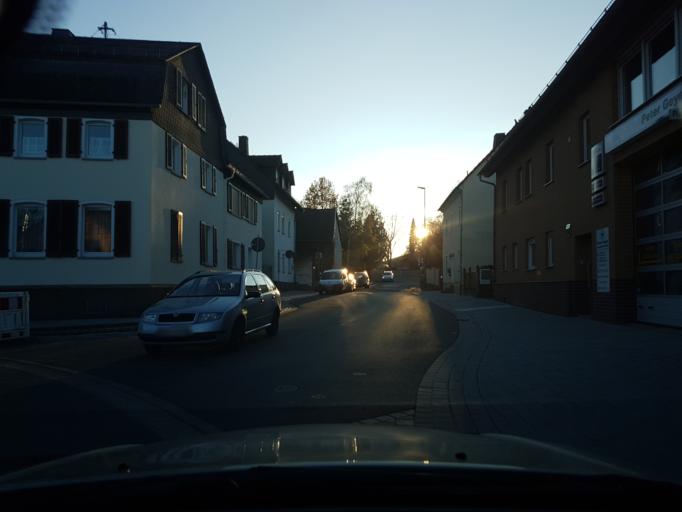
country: DE
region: Hesse
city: Taunusstein
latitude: 50.1538
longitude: 8.1861
